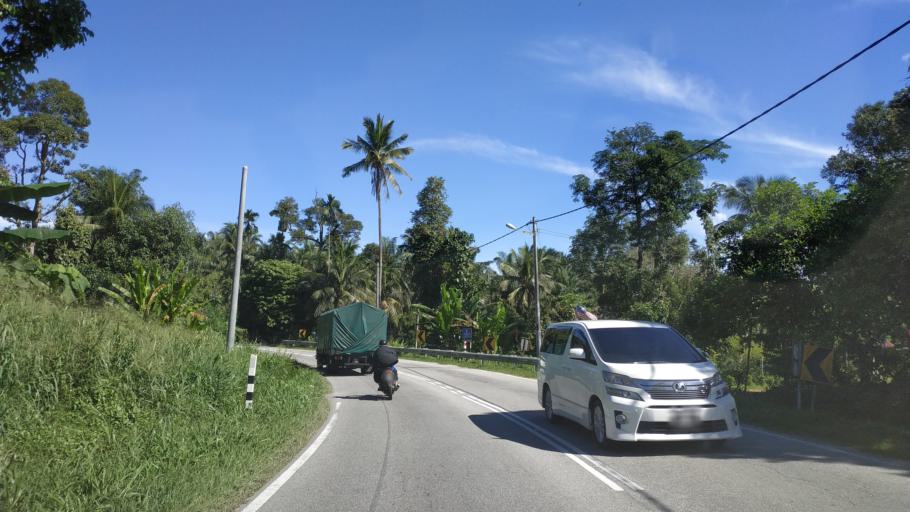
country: MY
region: Kedah
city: Kulim
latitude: 5.3087
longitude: 100.5406
